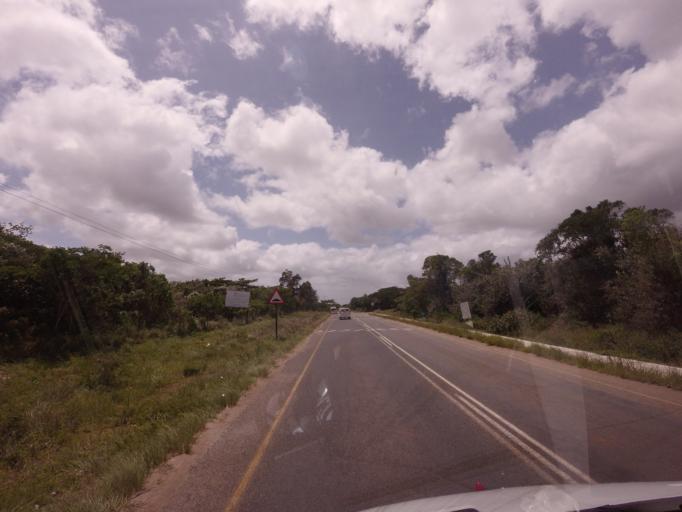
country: ZA
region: KwaZulu-Natal
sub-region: uMkhanyakude District Municipality
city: Mtubatuba
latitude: -28.3760
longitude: 32.3765
